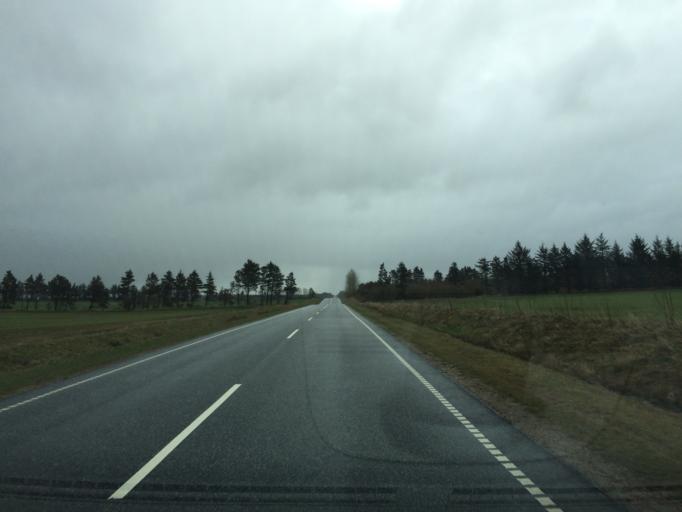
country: DK
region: Central Jutland
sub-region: Ringkobing-Skjern Kommune
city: Videbaek
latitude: 56.1880
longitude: 8.6140
